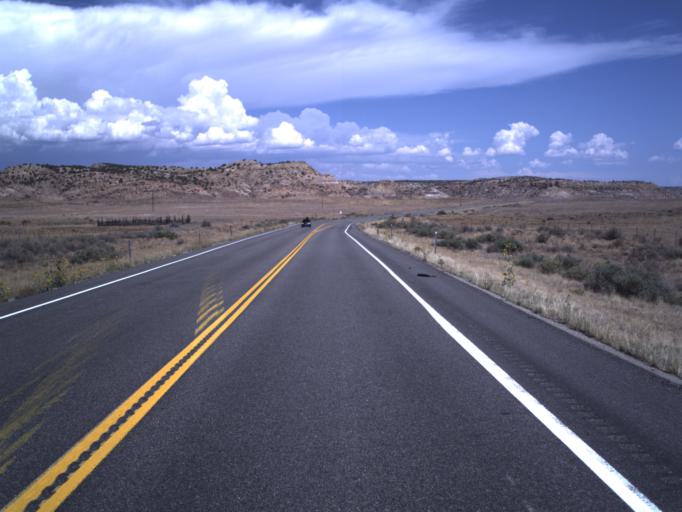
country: US
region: Utah
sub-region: San Juan County
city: Blanding
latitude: 37.4073
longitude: -109.4894
